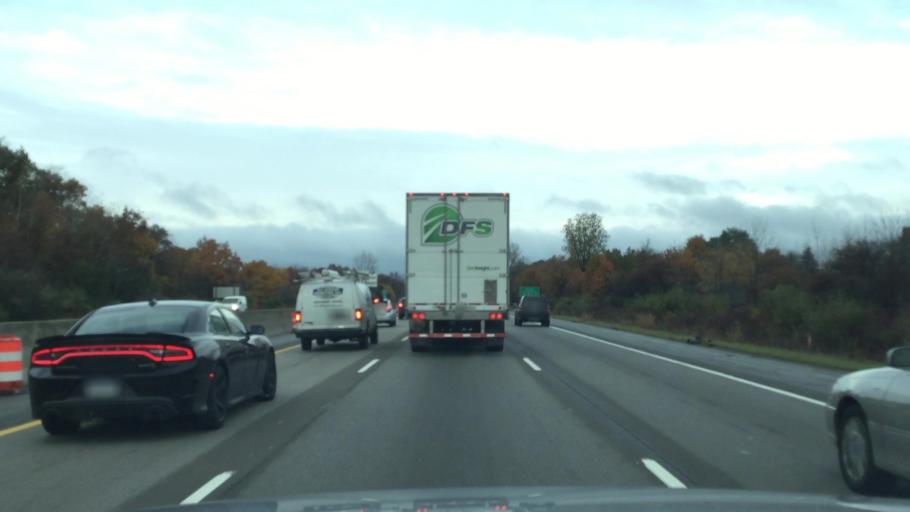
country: US
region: Michigan
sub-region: Washtenaw County
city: Ypsilanti
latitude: 42.2247
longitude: -83.6684
